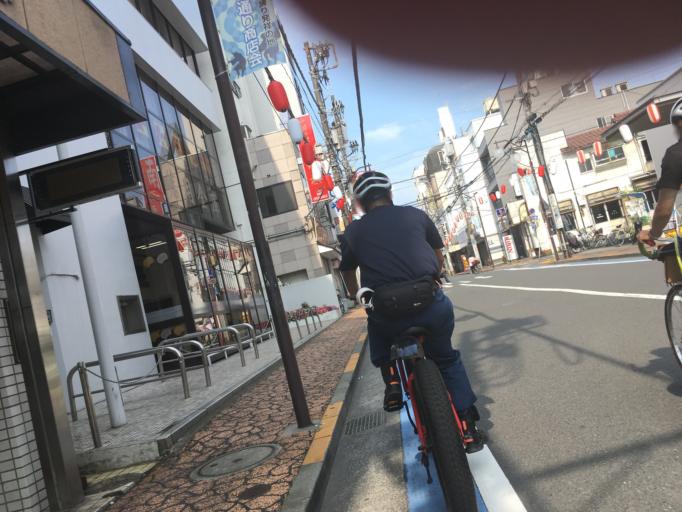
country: JP
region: Kanagawa
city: Minami-rinkan
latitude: 35.4711
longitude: 139.4633
